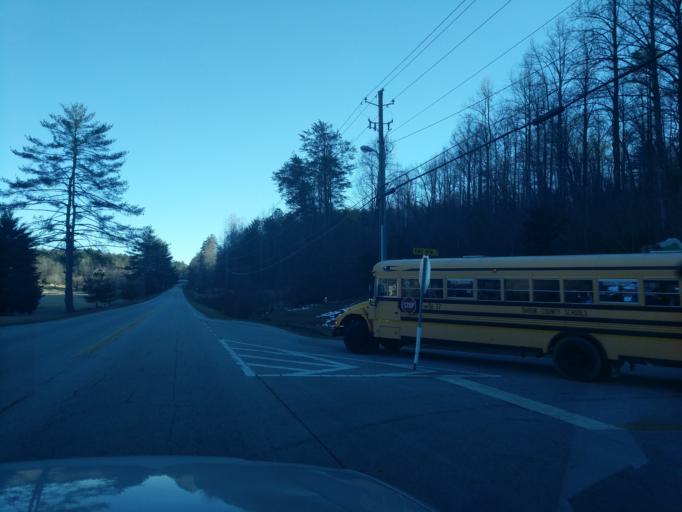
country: US
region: Georgia
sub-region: Rabun County
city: Clayton
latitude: 34.8585
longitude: -83.3711
